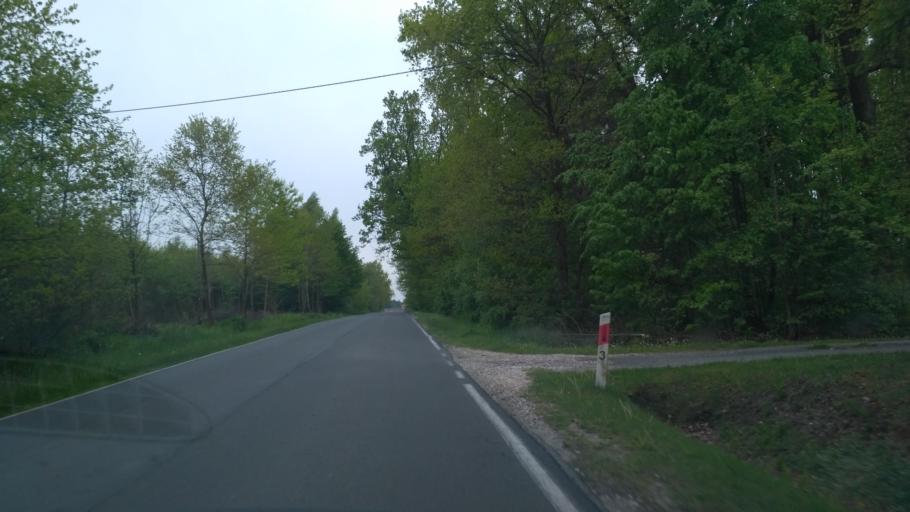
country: PL
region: Subcarpathian Voivodeship
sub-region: Powiat ropczycko-sedziszowski
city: Sedziszow Malopolski
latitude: 50.1297
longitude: 21.7540
